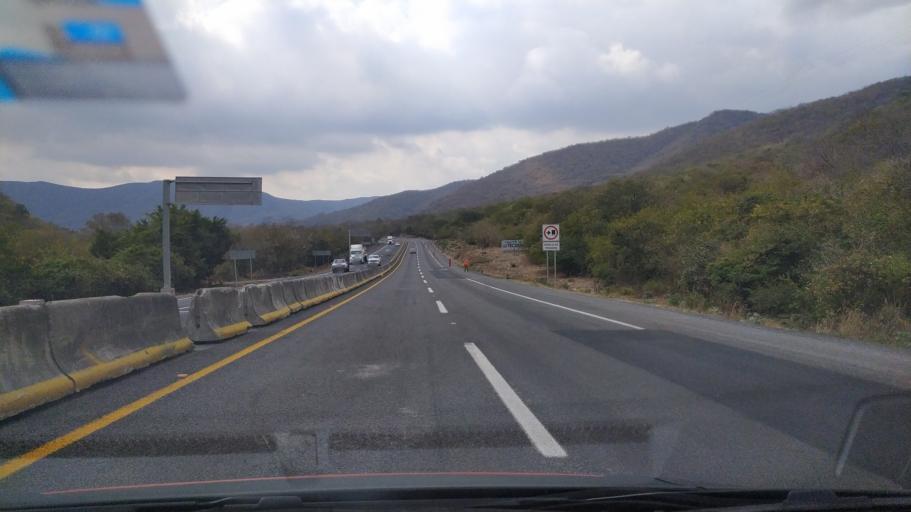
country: MX
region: Colima
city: Ixtlahuacan
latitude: 19.0224
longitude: -103.8089
